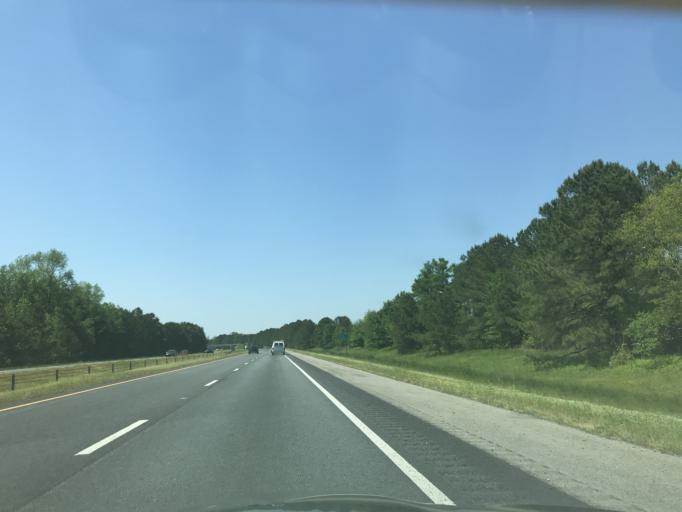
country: US
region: North Carolina
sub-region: Johnston County
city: Benson
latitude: 35.3356
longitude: -78.4605
